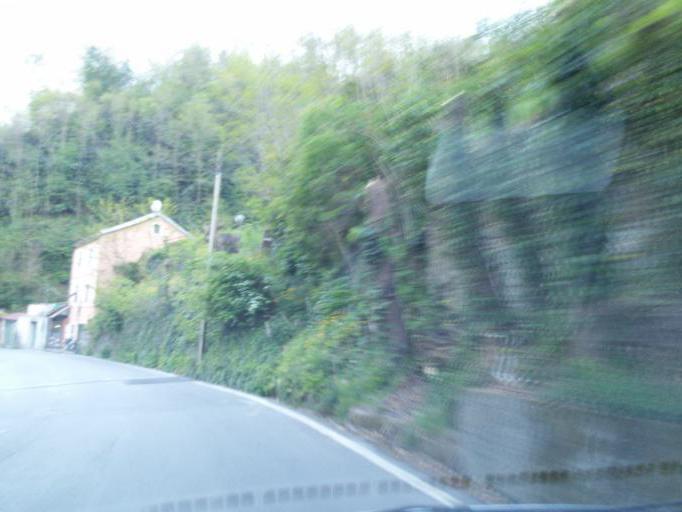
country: IT
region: Liguria
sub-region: Provincia di Genova
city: Santa Marta
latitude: 44.4725
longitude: 8.8911
